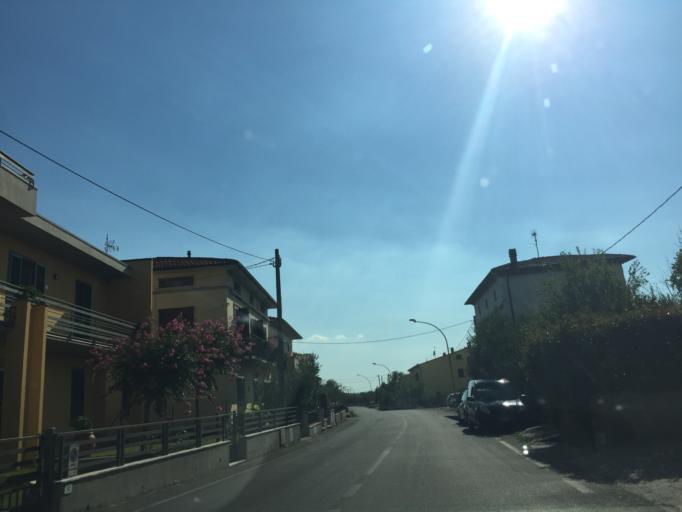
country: IT
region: Tuscany
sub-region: Provincia di Pistoia
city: San Rocco
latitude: 43.8215
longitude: 10.8693
